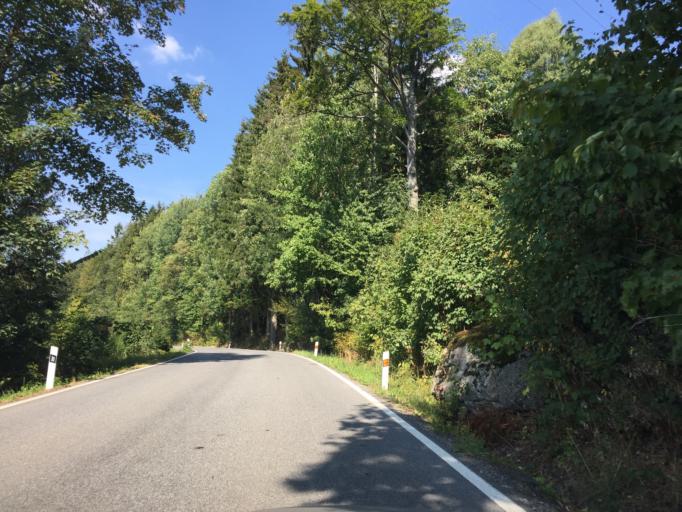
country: CZ
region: Liberecky
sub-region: Okres Jablonec nad Nisou
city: Janov nad Nisou
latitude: 50.7858
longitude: 15.1638
